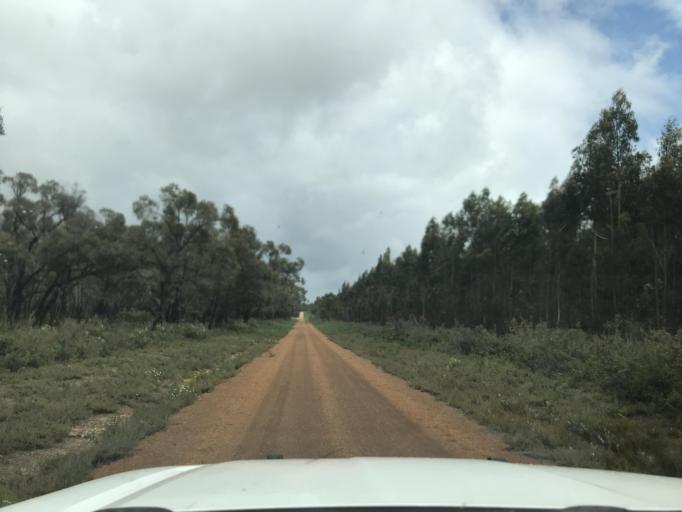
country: AU
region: South Australia
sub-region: Wattle Range
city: Penola
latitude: -37.2934
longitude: 141.2999
